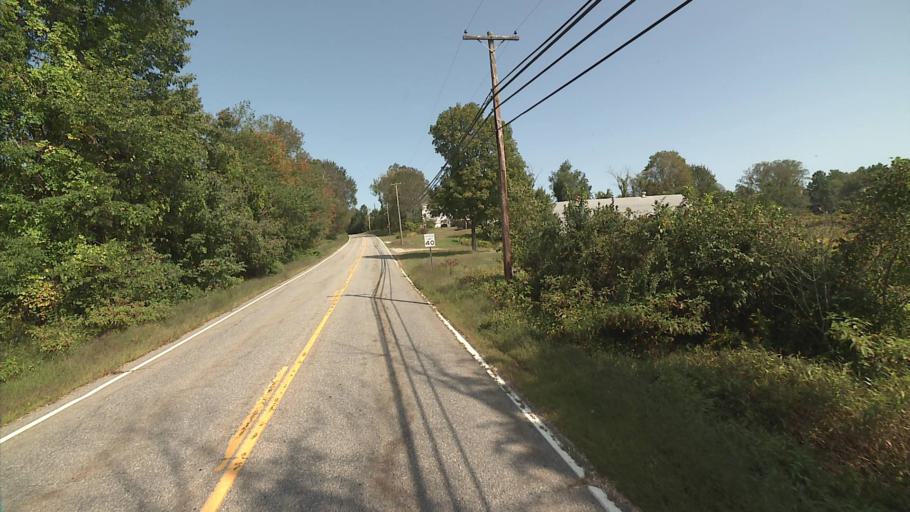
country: US
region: Connecticut
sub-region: Windham County
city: Putnam
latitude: 41.8622
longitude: -71.9592
